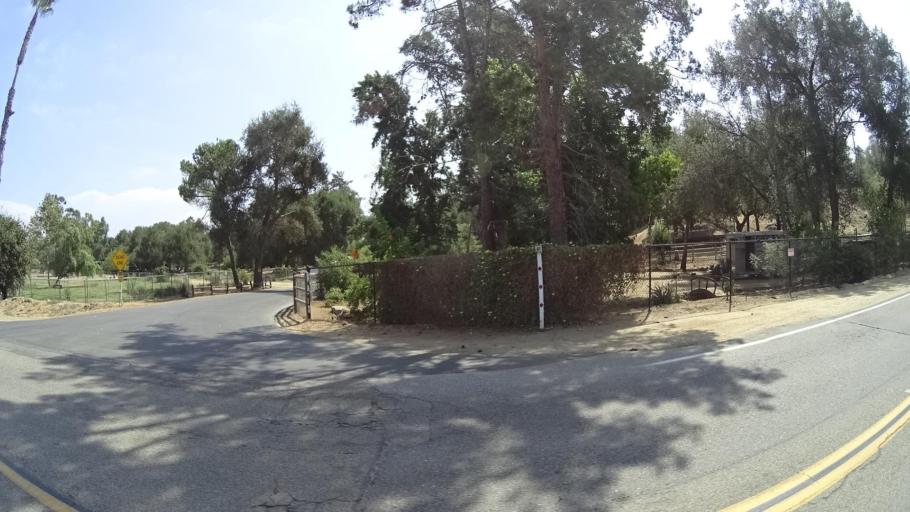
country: US
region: California
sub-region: San Diego County
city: Fallbrook
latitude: 33.3601
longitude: -117.2276
